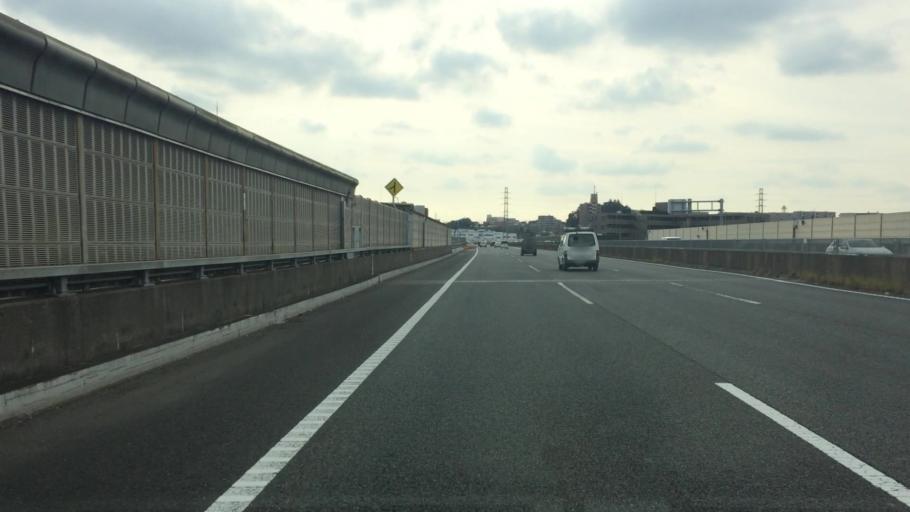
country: JP
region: Tokyo
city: Chofugaoka
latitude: 35.5910
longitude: 139.6243
